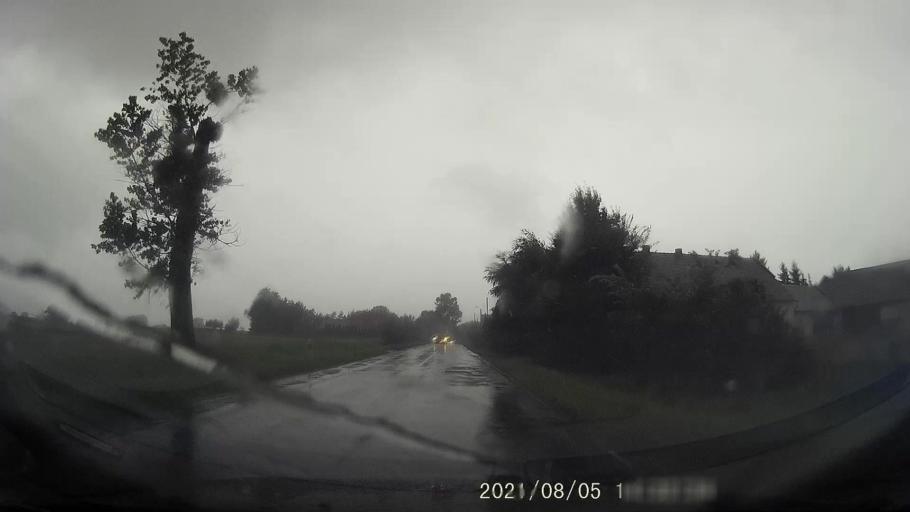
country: PL
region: Opole Voivodeship
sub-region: Powiat nyski
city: Korfantow
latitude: 50.4769
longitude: 17.6573
